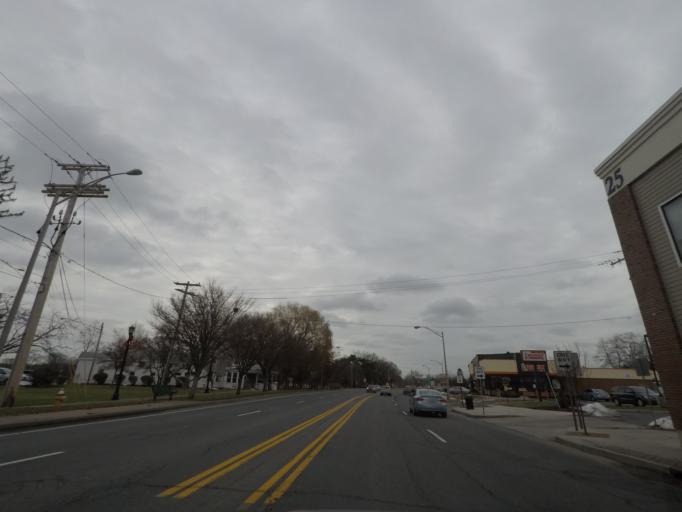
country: US
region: New York
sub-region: Schenectady County
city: Scotia
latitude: 42.8245
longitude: -73.9603
